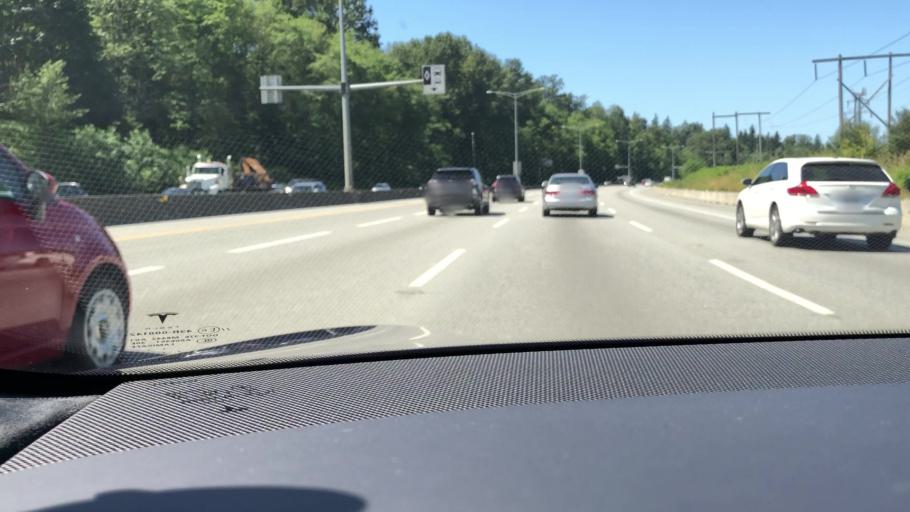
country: CA
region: British Columbia
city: New Westminster
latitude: 49.2370
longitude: -122.9229
